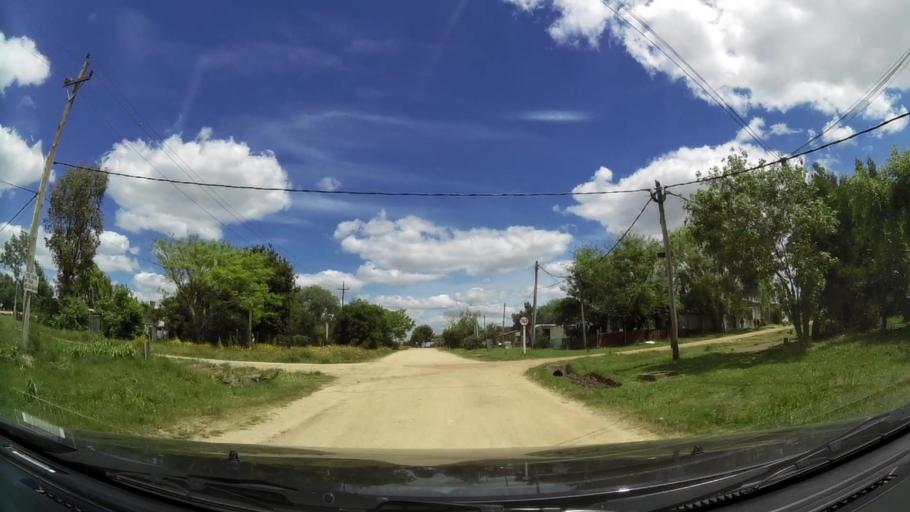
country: UY
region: Canelones
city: Colonia Nicolich
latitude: -34.7941
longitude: -55.9907
